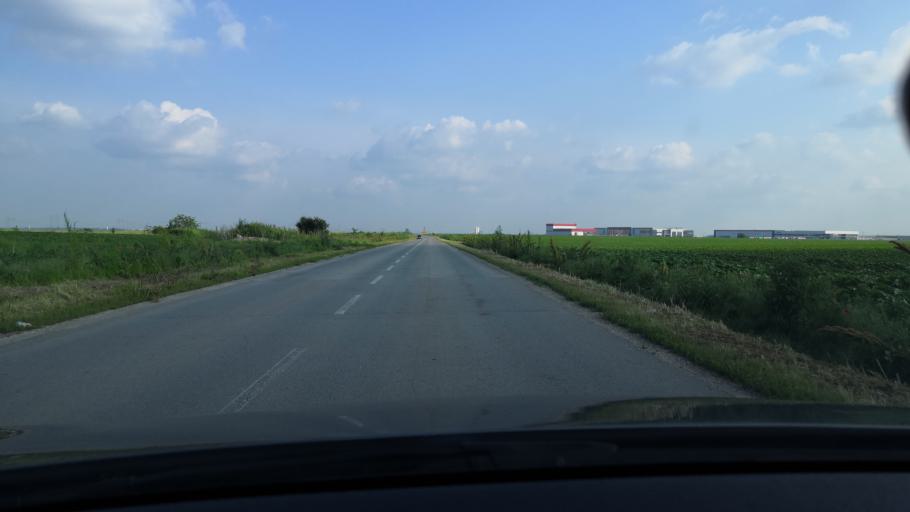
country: RS
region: Autonomna Pokrajina Vojvodina
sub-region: Sremski Okrug
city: Ingija
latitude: 45.0716
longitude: 20.1256
